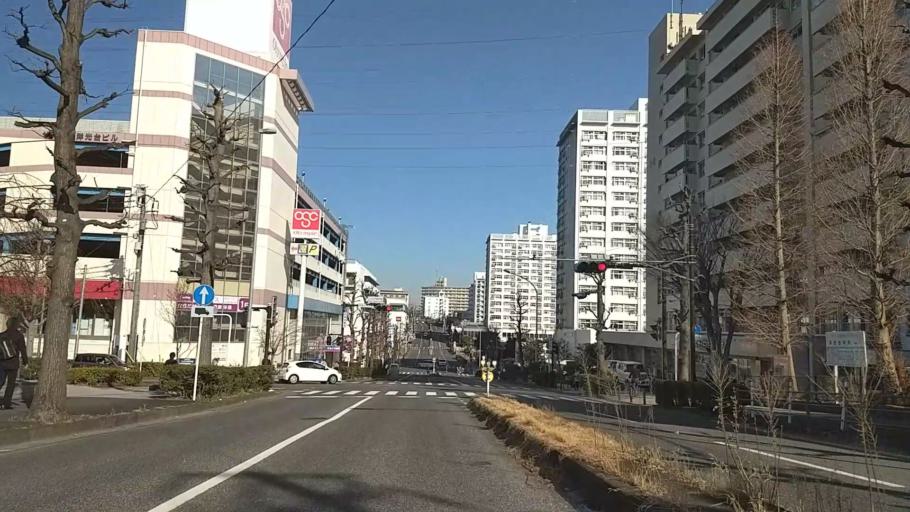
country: JP
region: Kanagawa
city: Kamakura
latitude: 35.3767
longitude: 139.5964
